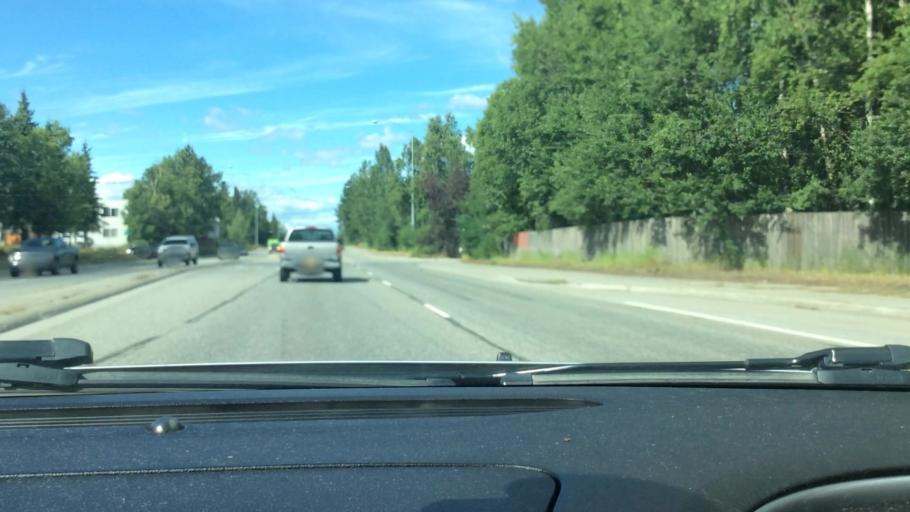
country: US
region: Alaska
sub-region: Anchorage Municipality
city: Anchorage
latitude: 61.1821
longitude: -149.7781
